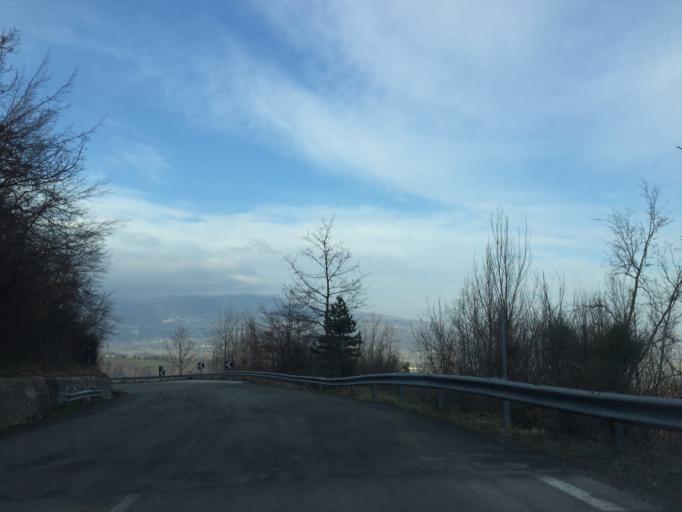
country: IT
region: Molise
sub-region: Provincia di Campobasso
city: San Massimo
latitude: 41.4845
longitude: 14.4097
